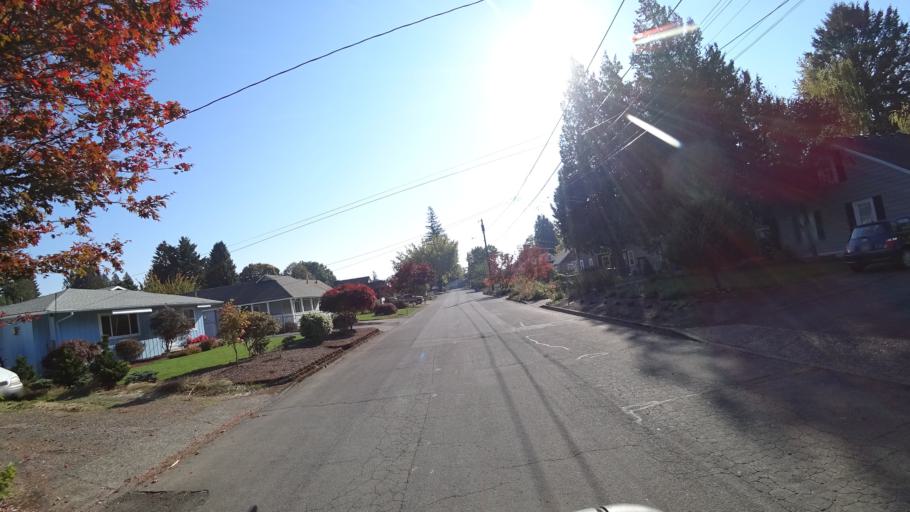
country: US
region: Oregon
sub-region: Multnomah County
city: Gresham
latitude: 45.5030
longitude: -122.4492
